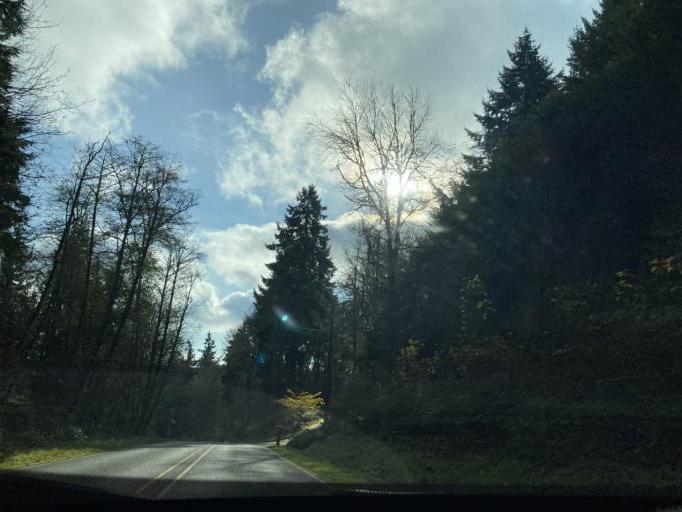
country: US
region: Washington
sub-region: Island County
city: Langley
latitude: 47.9588
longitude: -122.4412
